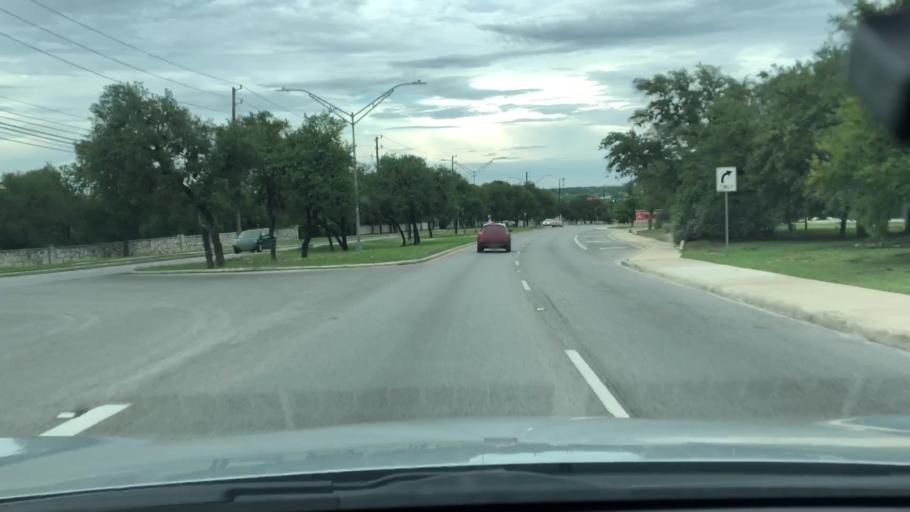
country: US
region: Texas
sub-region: Bexar County
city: Leon Valley
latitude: 29.4753
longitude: -98.6690
